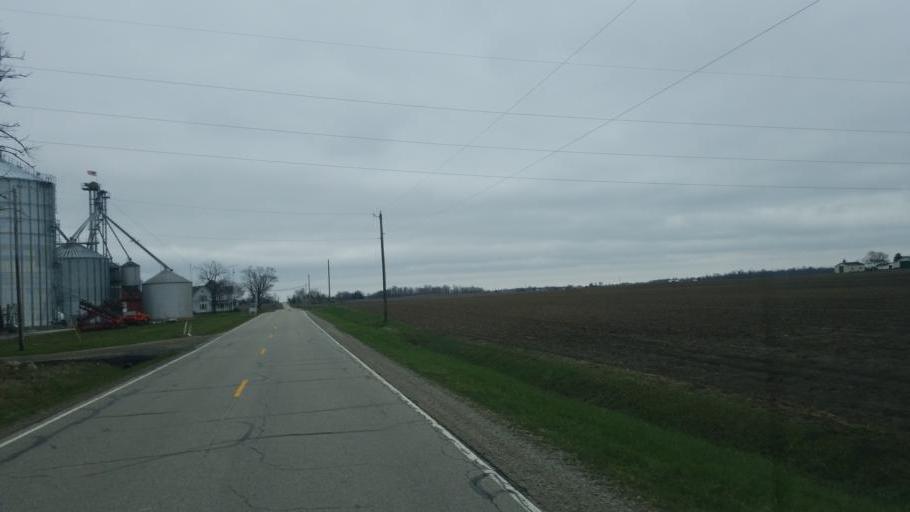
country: US
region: Ohio
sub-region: Crawford County
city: Bucyrus
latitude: 40.8532
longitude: -82.9402
